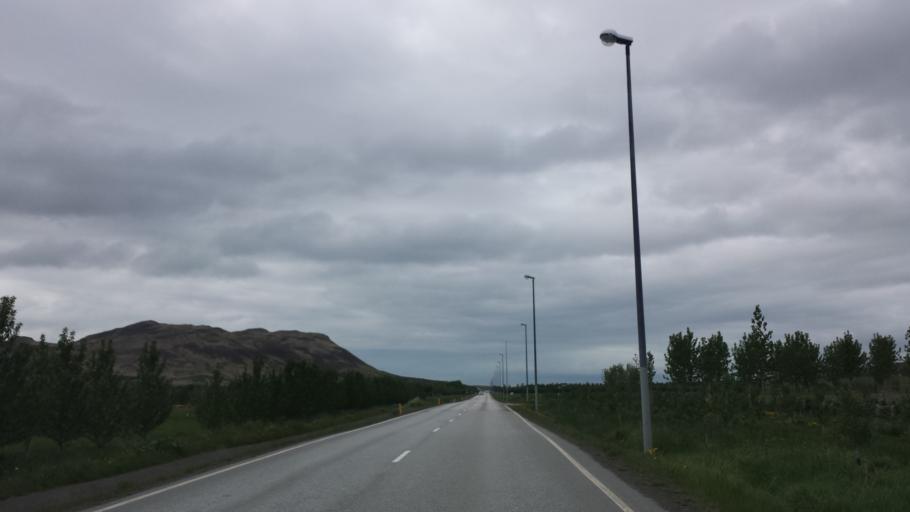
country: IS
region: Capital Region
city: Mosfellsbaer
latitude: 64.1808
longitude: -21.6043
